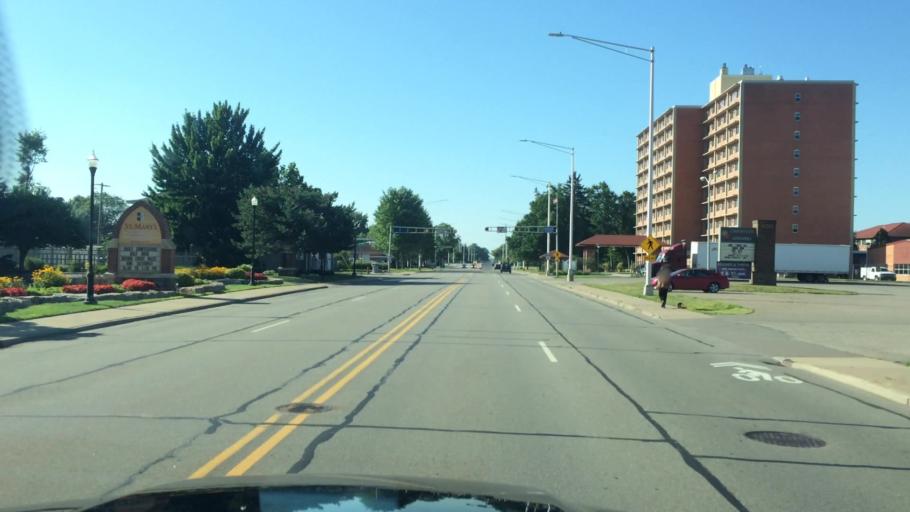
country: US
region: Wisconsin
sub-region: Marathon County
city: Wausau
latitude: 44.9537
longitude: -89.6236
